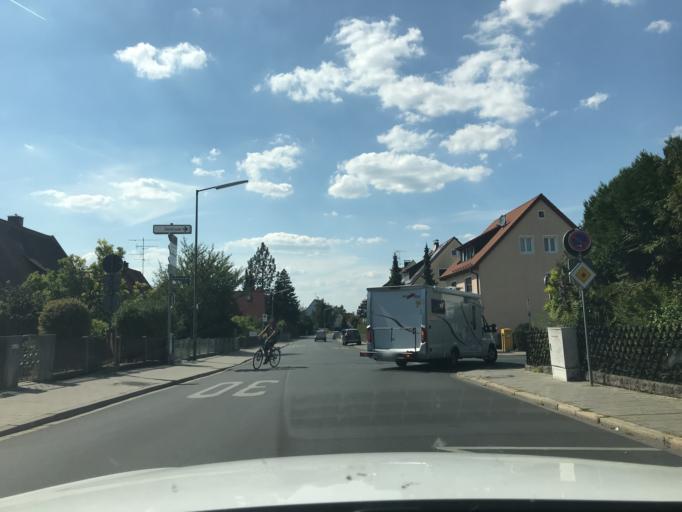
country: DE
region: Bavaria
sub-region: Regierungsbezirk Mittelfranken
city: Erlangen
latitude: 49.5661
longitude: 11.0013
